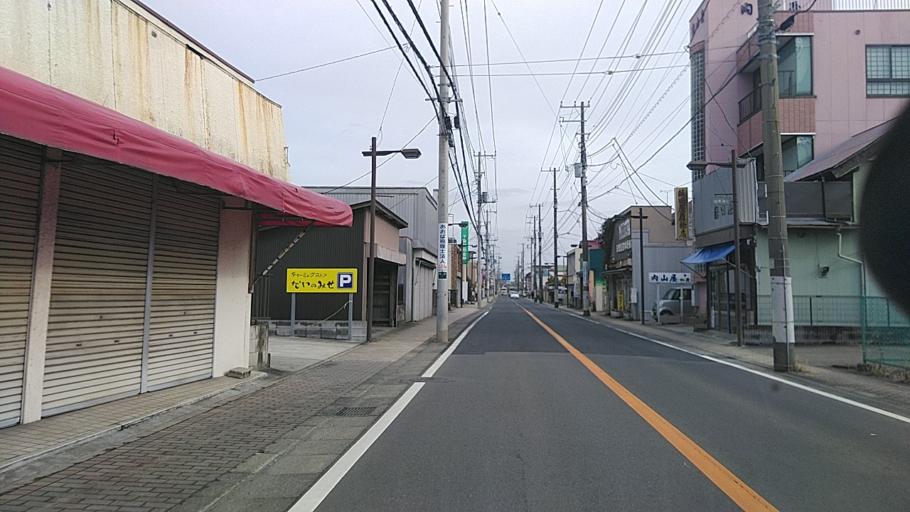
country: JP
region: Chiba
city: Togane
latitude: 35.5622
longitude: 140.3635
